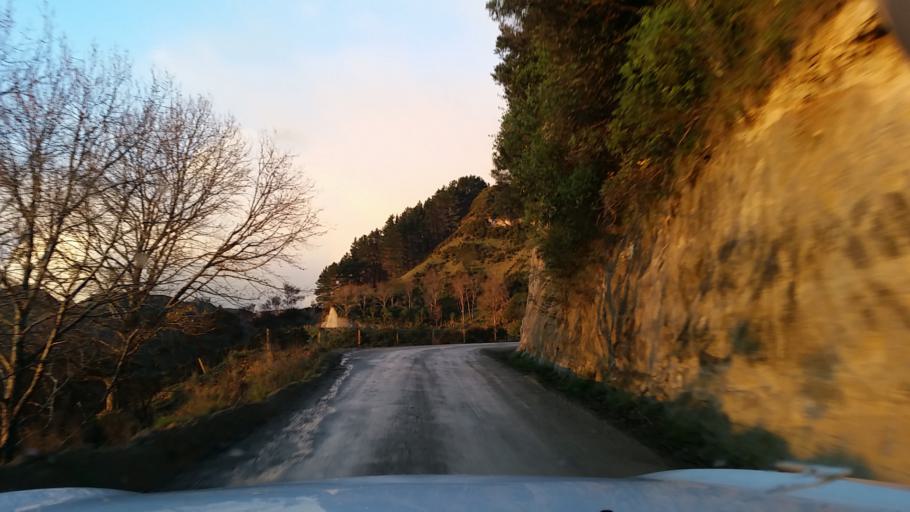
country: NZ
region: Manawatu-Wanganui
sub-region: Wanganui District
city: Wanganui
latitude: -39.7657
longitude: 174.8726
